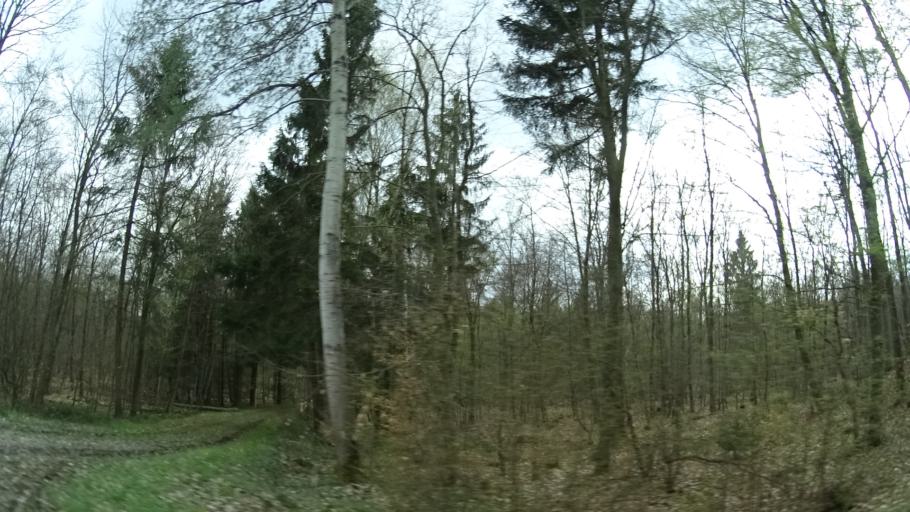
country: DE
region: Rheinland-Pfalz
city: Seesbach
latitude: 49.8705
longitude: 7.5619
